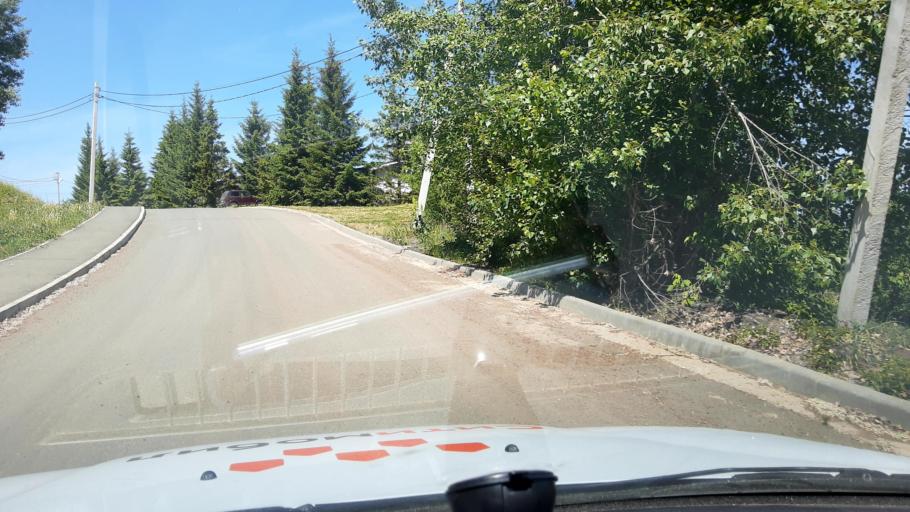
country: RU
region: Bashkortostan
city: Ufa
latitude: 54.6048
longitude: 55.9658
